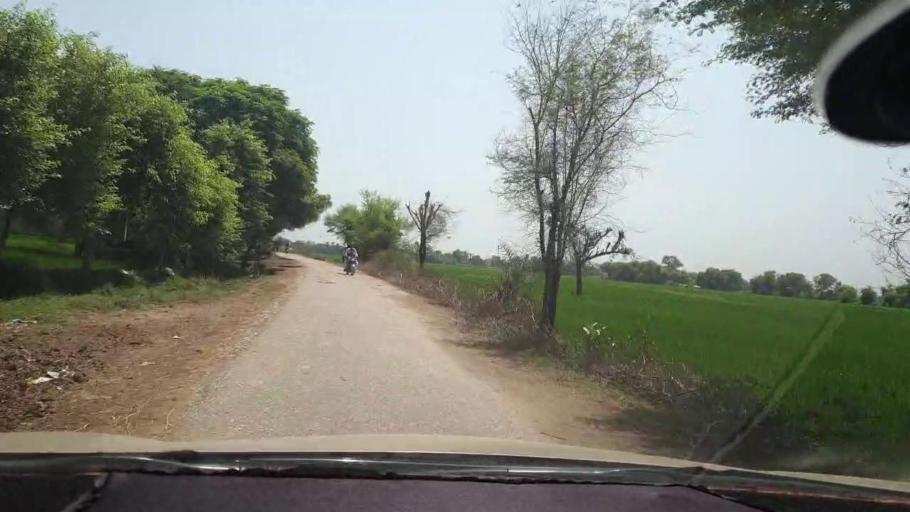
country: PK
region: Sindh
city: Kambar
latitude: 27.6787
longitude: 67.9403
